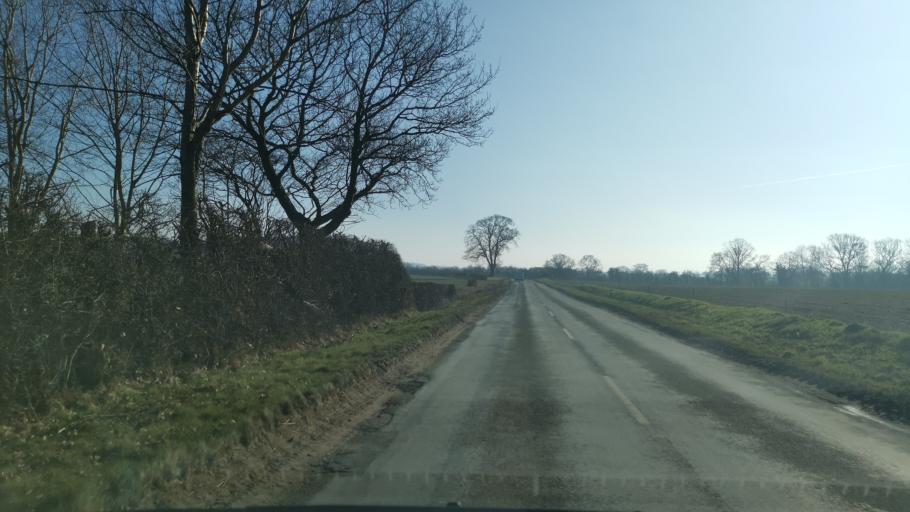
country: GB
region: England
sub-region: City of York
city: Murton
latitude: 53.9836
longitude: -1.0107
